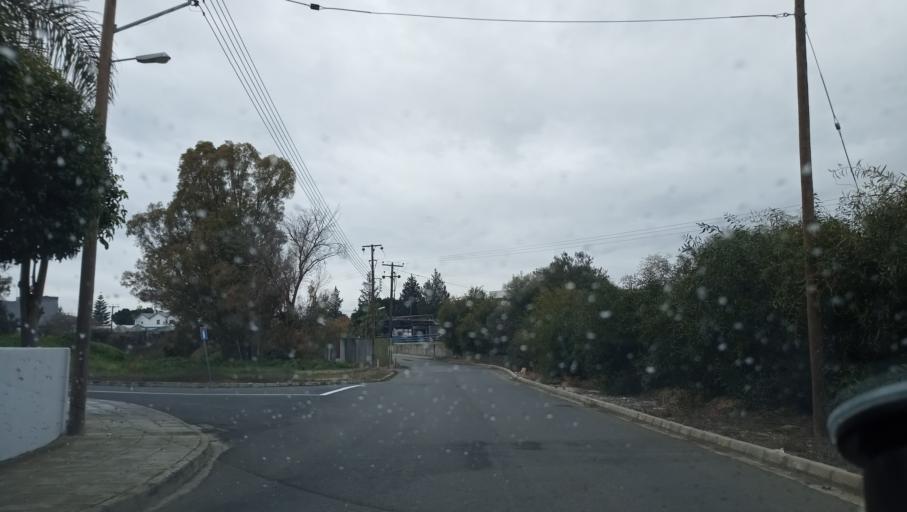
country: CY
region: Lefkosia
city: Kato Deftera
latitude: 35.0884
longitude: 33.2870
